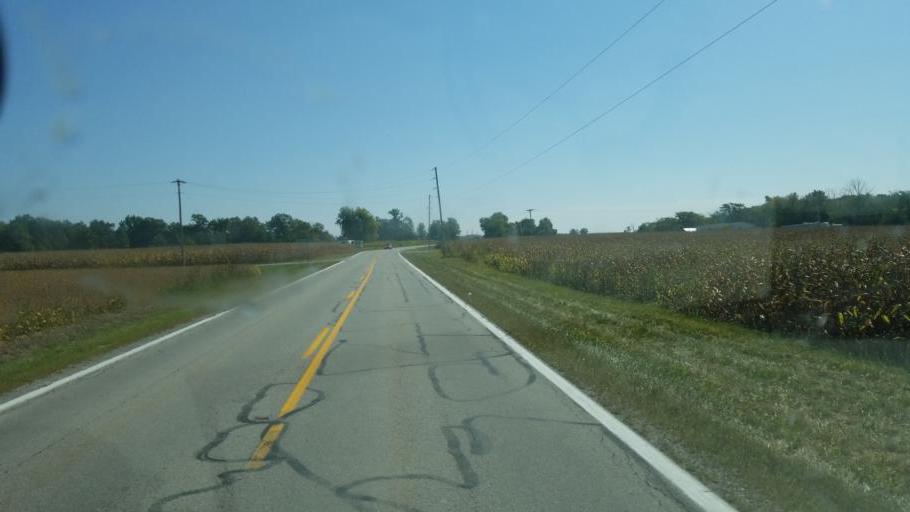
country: US
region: Ohio
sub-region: Marion County
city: Marion
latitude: 40.6350
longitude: -83.2710
